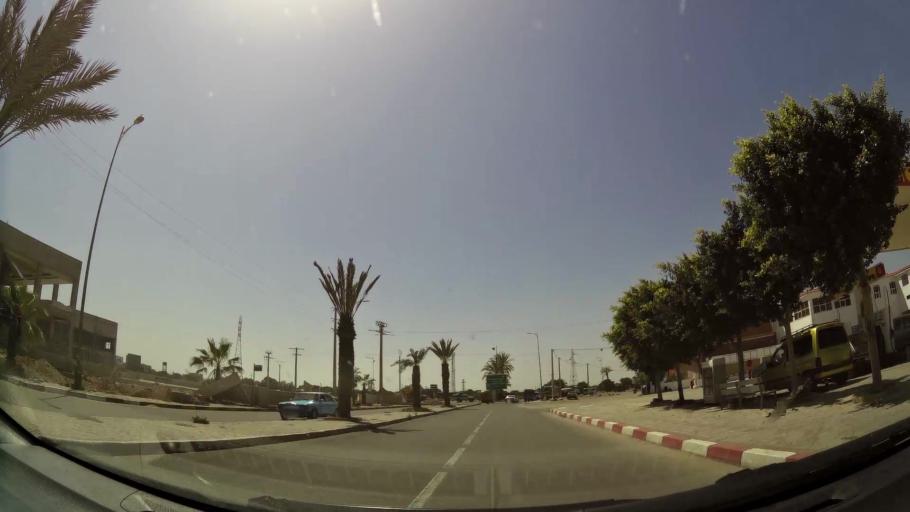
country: MA
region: Souss-Massa-Draa
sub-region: Inezgane-Ait Mellou
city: Inezgane
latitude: 30.3111
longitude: -9.5027
